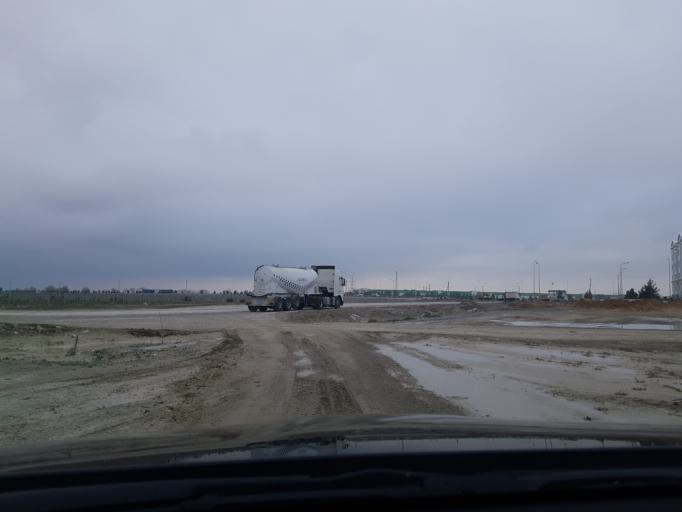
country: TM
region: Ahal
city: Abadan
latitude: 38.1636
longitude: 57.9297
